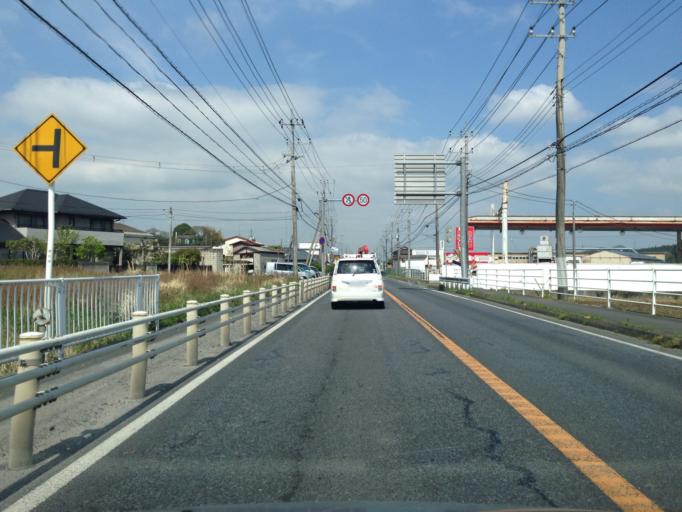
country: JP
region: Ibaraki
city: Kasama
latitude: 36.3725
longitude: 140.2154
